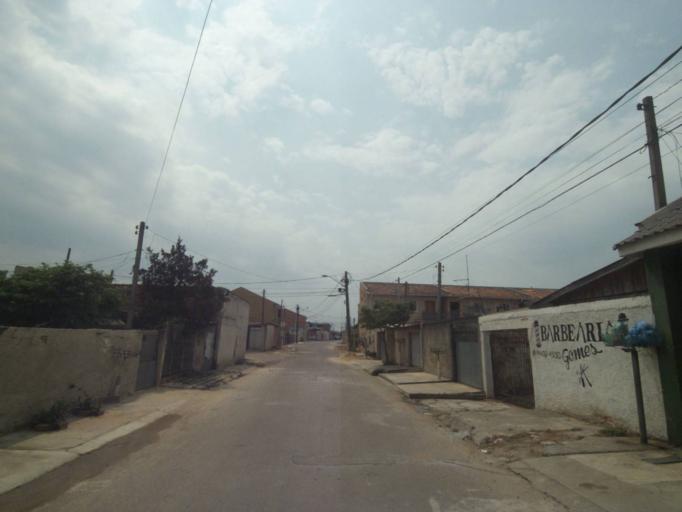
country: BR
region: Parana
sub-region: Sao Jose Dos Pinhais
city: Sao Jose dos Pinhais
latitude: -25.4951
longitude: -49.2011
